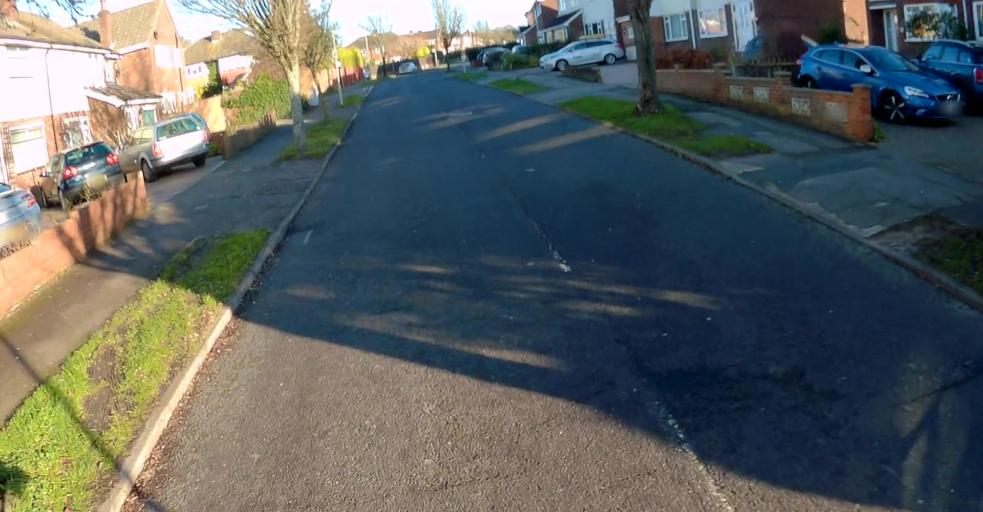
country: GB
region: England
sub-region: Hampshire
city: Basingstoke
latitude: 51.2512
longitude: -1.0963
